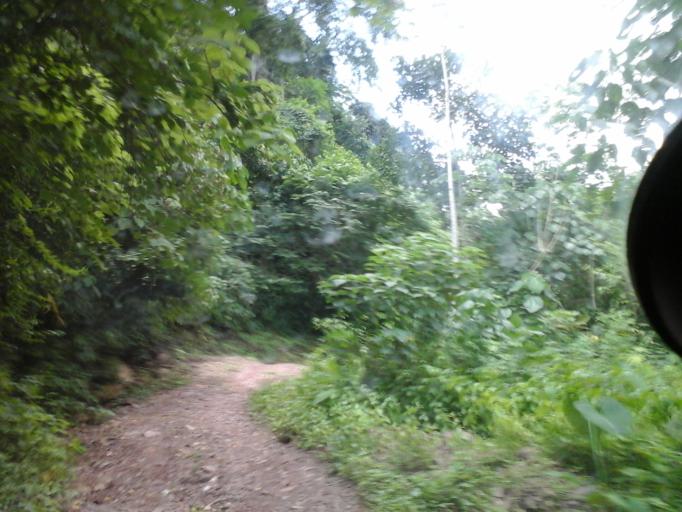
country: CO
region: Cesar
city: Manaure Balcon del Cesar
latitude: 10.2915
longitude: -73.0788
